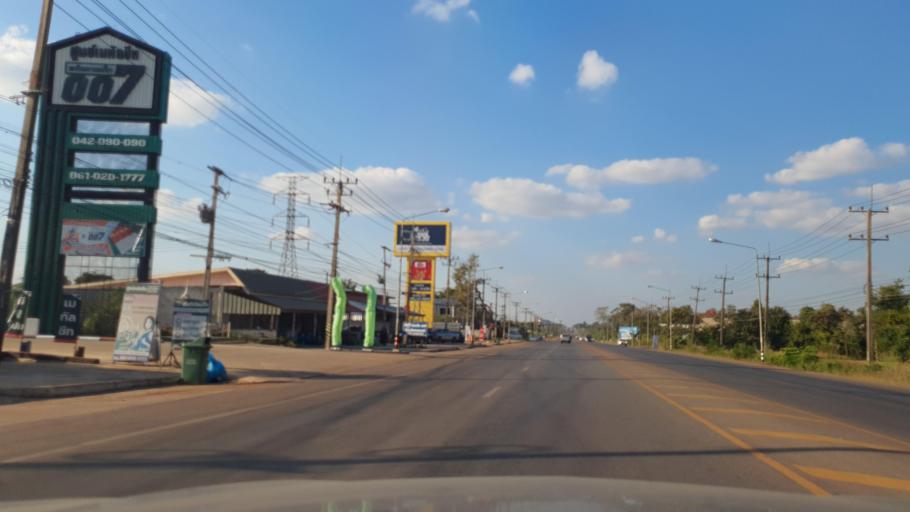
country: TH
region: Sakon Nakhon
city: Sakon Nakhon
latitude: 17.1509
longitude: 104.1068
